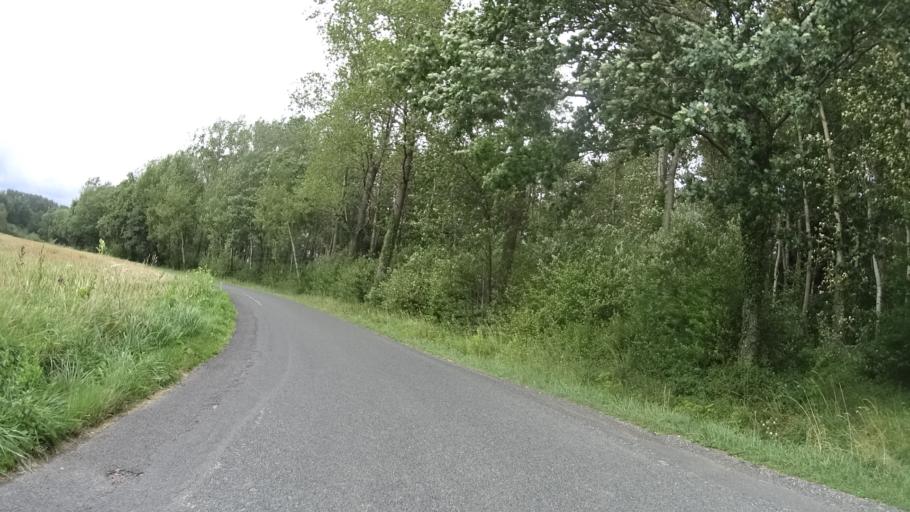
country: FR
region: Lorraine
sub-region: Departement de la Moselle
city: Sarrebourg
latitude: 48.6973
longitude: 7.0648
